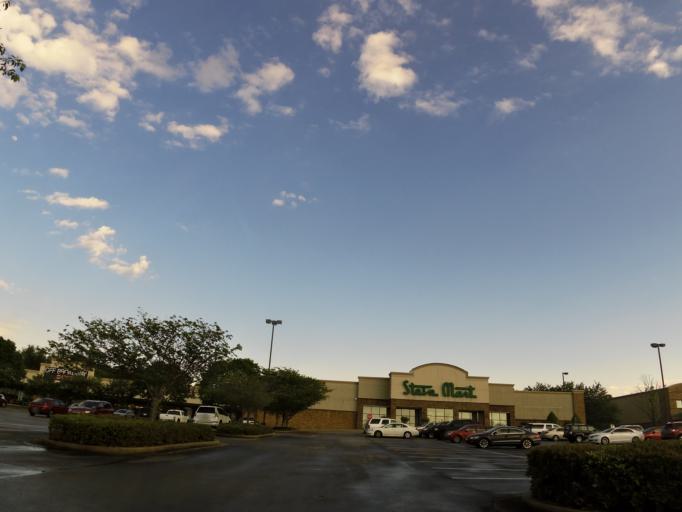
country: US
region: Tennessee
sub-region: Blount County
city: Louisville
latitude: 35.9250
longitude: -84.0317
